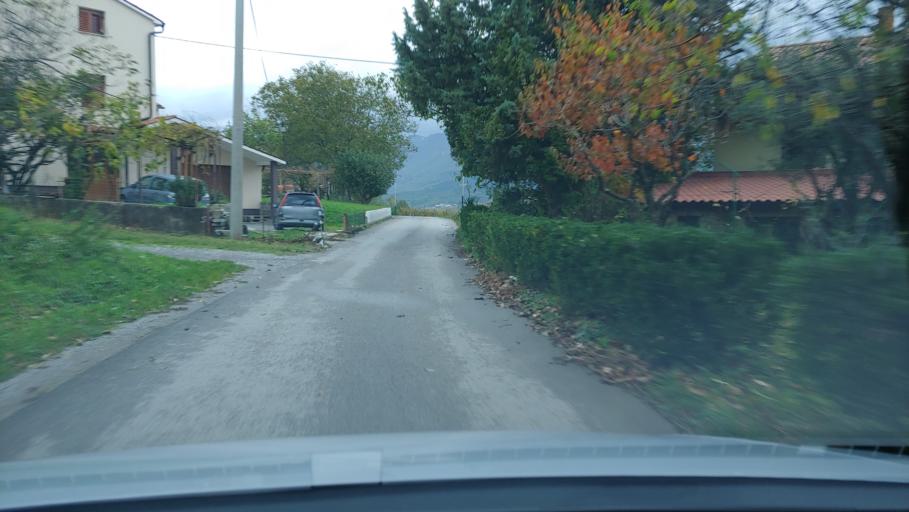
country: SI
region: Vipava
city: Vipava
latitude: 45.8408
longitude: 13.9394
